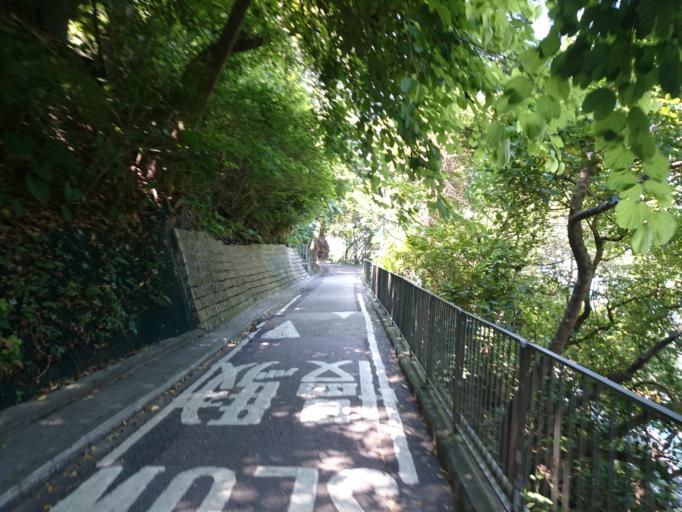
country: HK
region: Central and Western
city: Central
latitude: 22.2751
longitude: 114.1633
